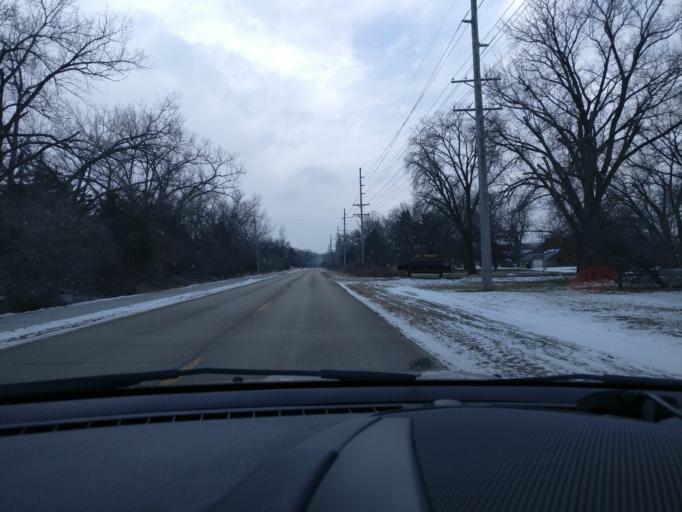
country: US
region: Nebraska
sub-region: Dodge County
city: Fremont
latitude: 41.4233
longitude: -96.5215
